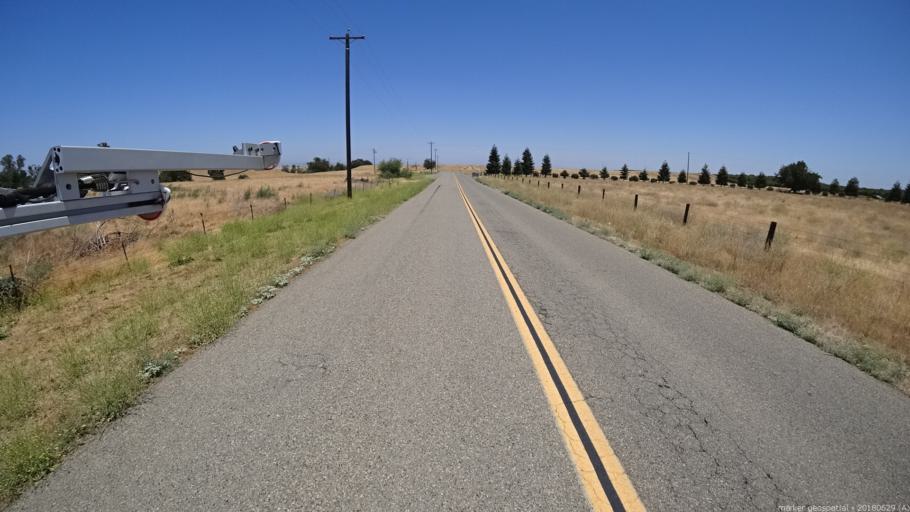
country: US
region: California
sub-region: Madera County
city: Parksdale
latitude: 37.0117
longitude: -119.9666
